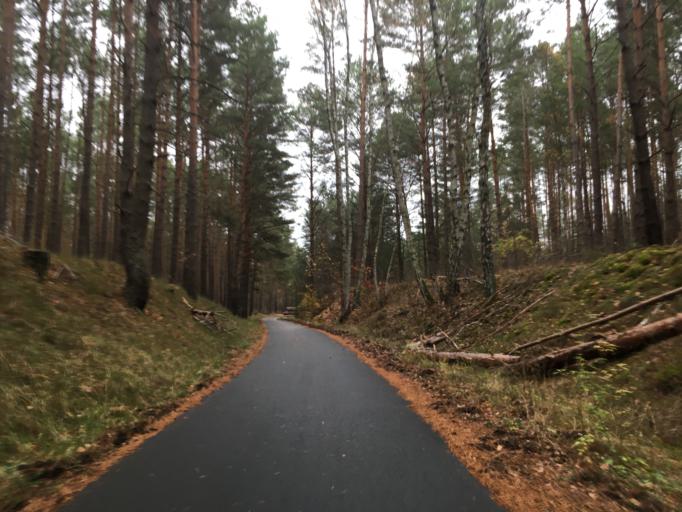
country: DE
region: Brandenburg
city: Mullrose
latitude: 52.2249
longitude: 14.4430
